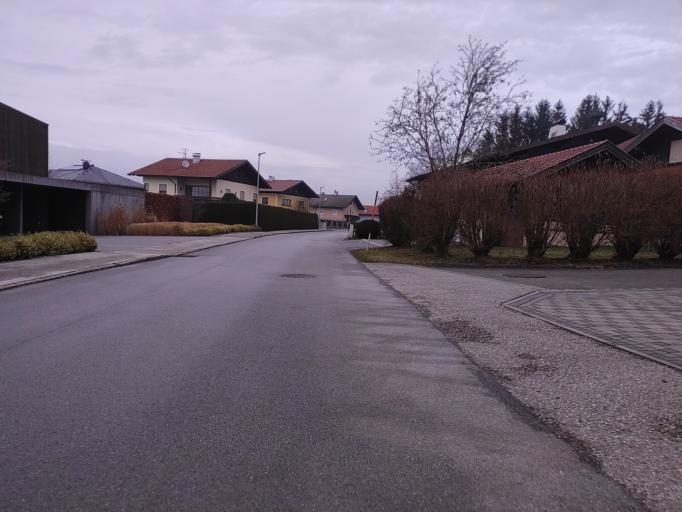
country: AT
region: Salzburg
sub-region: Politischer Bezirk Salzburg-Umgebung
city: Neumarkt am Wallersee
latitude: 47.9316
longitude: 13.2196
